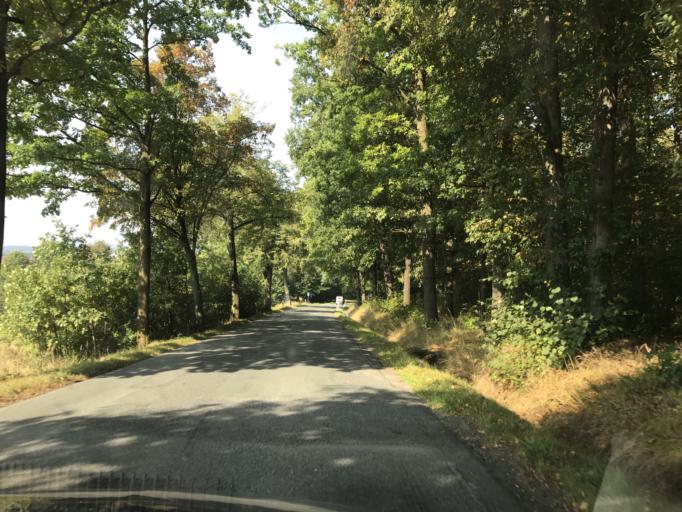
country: DE
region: Saxony
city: Lobau
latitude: 51.0868
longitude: 14.6824
